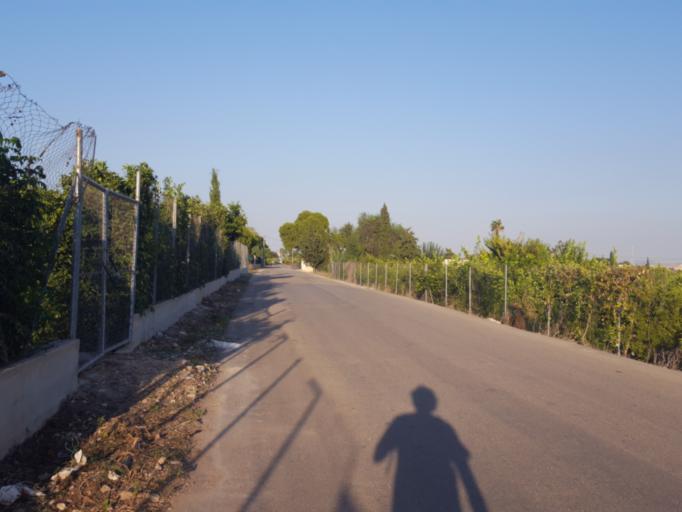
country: ES
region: Murcia
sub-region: Murcia
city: Murcia
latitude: 37.9954
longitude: -1.1725
